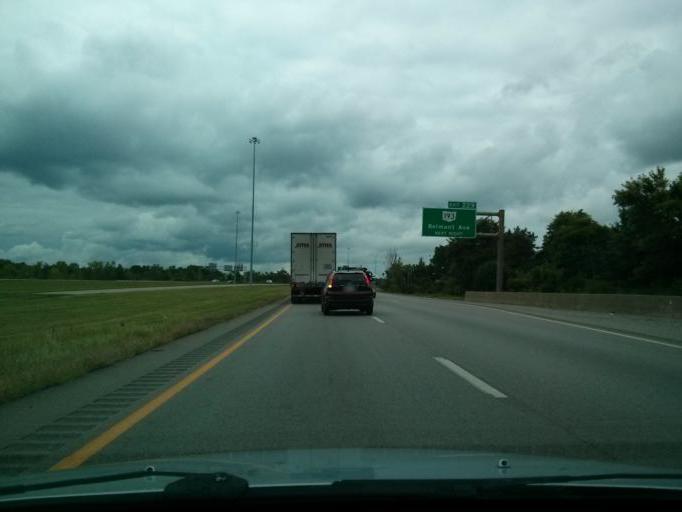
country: US
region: Ohio
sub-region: Trumbull County
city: Churchill
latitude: 41.1495
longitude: -80.6721
